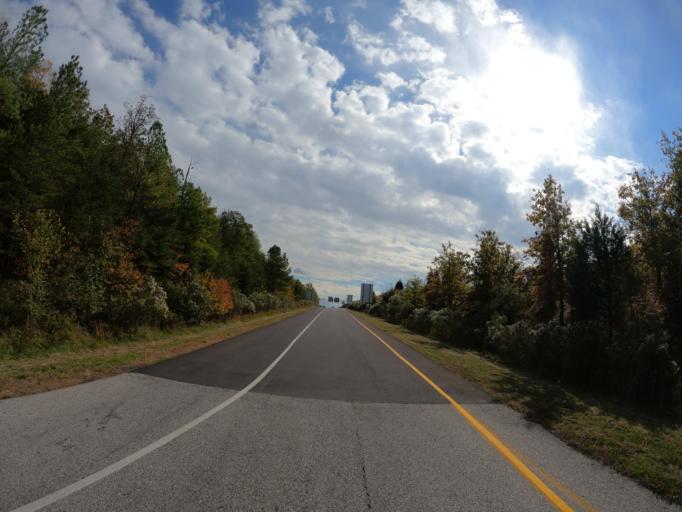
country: US
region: Maryland
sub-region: Anne Arundel County
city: Severn
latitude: 39.1582
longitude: -76.7164
